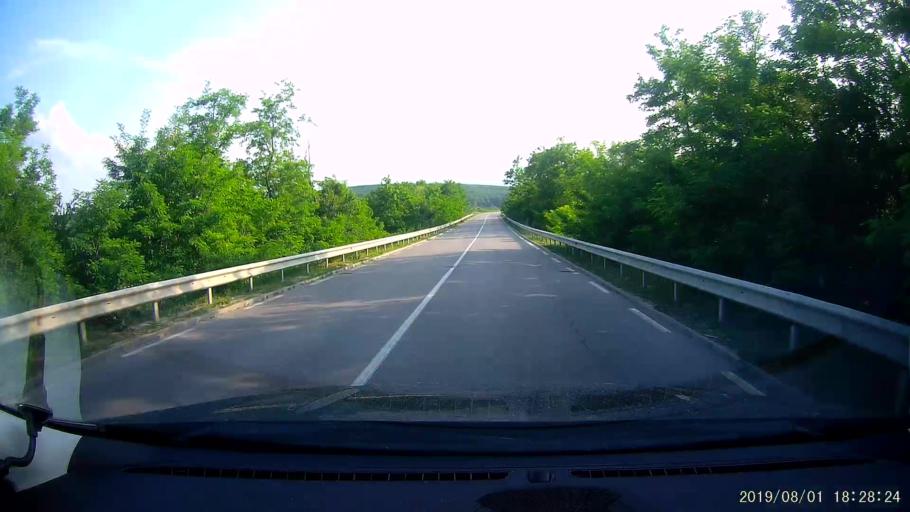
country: BG
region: Shumen
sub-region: Obshtina Venets
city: Venets
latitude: 43.5757
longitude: 26.9650
